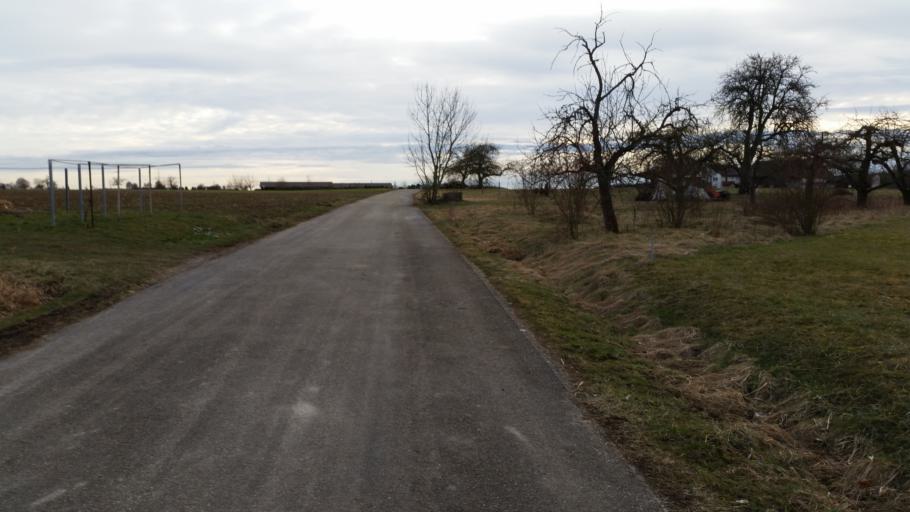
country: DE
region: Baden-Wuerttemberg
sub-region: Regierungsbezirk Stuttgart
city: Lochgau
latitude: 48.9977
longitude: 9.1032
